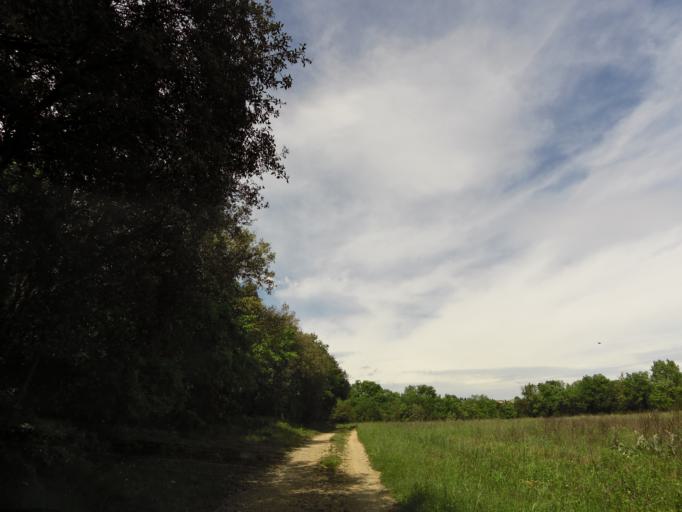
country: FR
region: Languedoc-Roussillon
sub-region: Departement du Gard
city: Quissac
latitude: 43.8824
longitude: 4.0296
